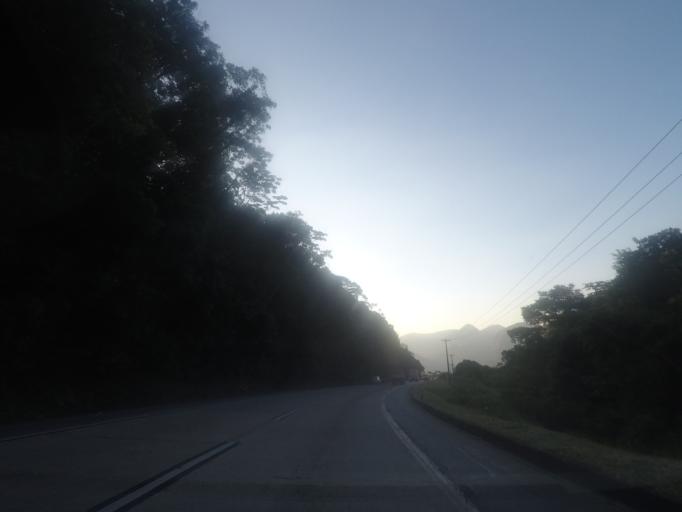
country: BR
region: Rio de Janeiro
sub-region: Petropolis
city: Petropolis
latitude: -22.5223
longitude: -43.2324
